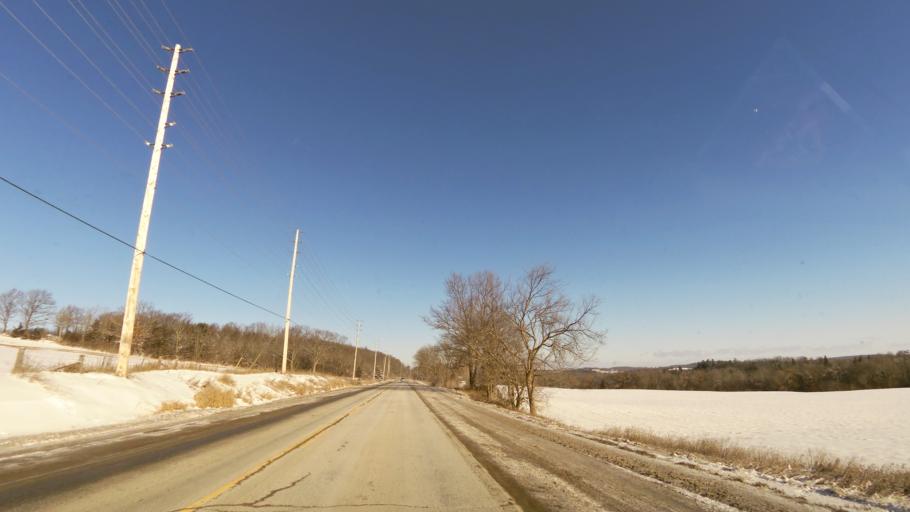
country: CA
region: Ontario
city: Quinte West
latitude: 44.2370
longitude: -77.8197
